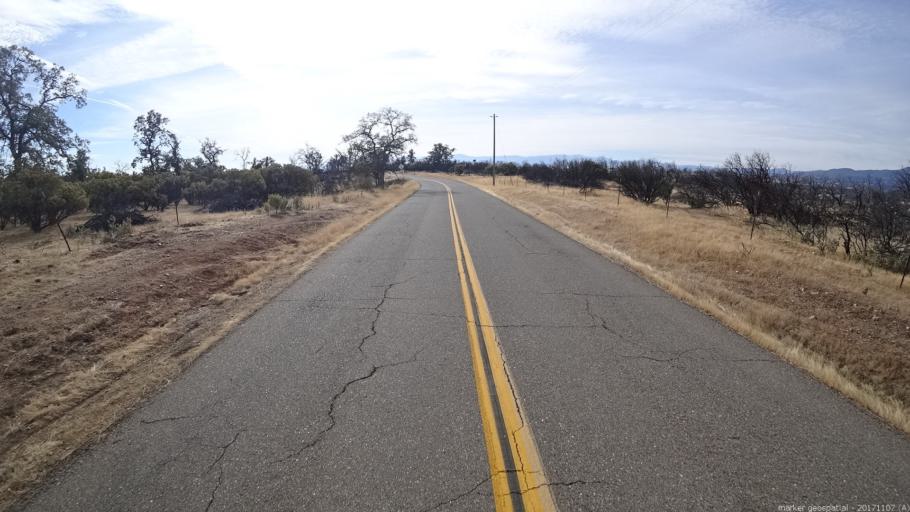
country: US
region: California
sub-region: Shasta County
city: Shasta
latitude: 40.4672
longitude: -122.5416
